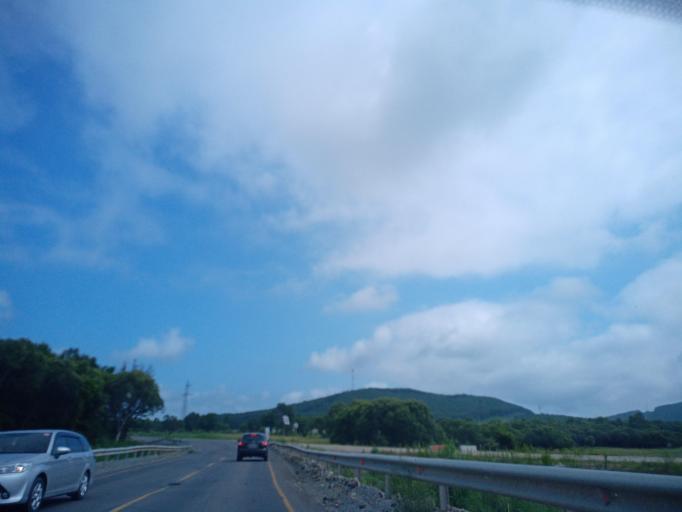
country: RU
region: Primorskiy
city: Dal'nerechensk
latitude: 46.0677
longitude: 133.8950
